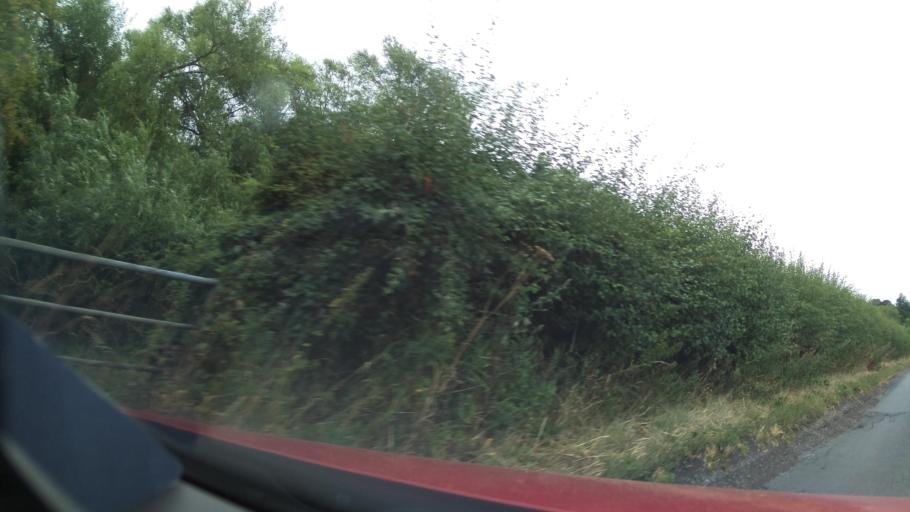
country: GB
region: England
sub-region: Derbyshire
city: Repton
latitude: 52.8263
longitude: -1.5391
